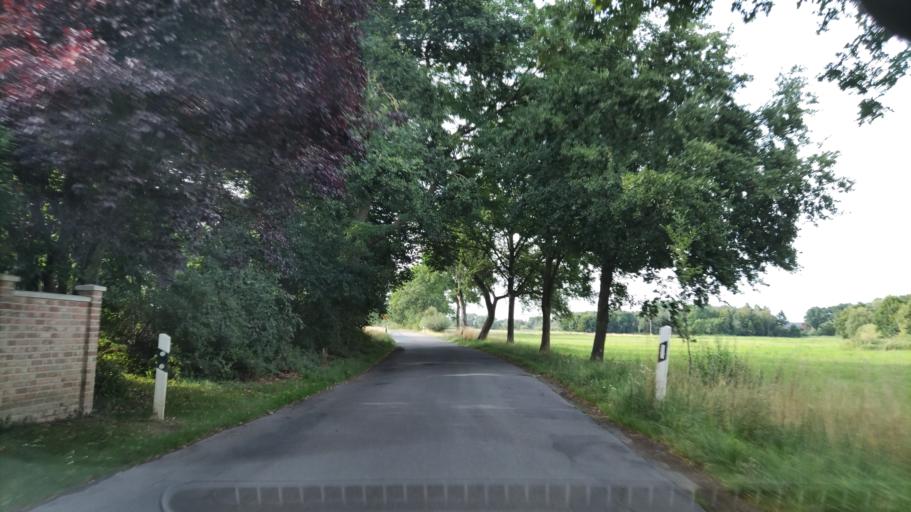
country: DE
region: Lower Saxony
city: Jameln
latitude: 53.0642
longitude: 11.1178
